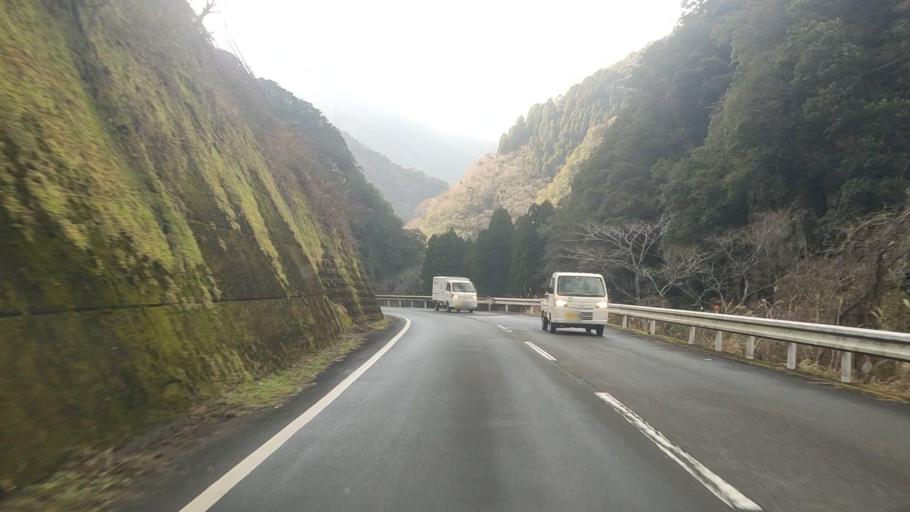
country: JP
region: Kumamoto
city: Hitoyoshi
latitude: 32.4267
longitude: 130.8571
